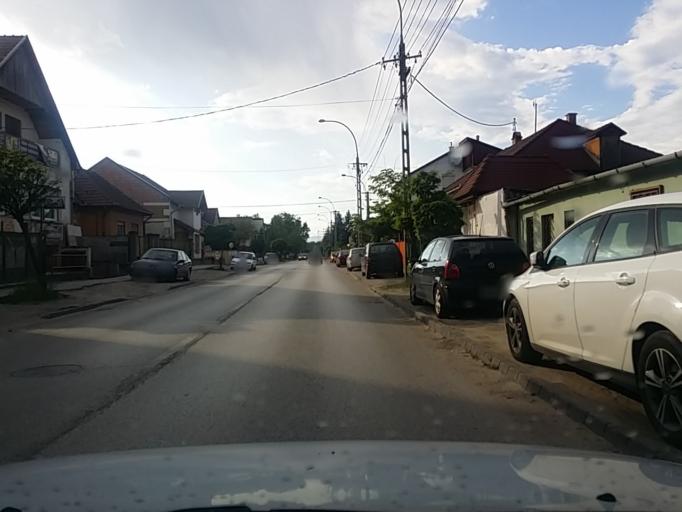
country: HU
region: Pest
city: Fot
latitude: 47.6266
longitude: 19.1826
